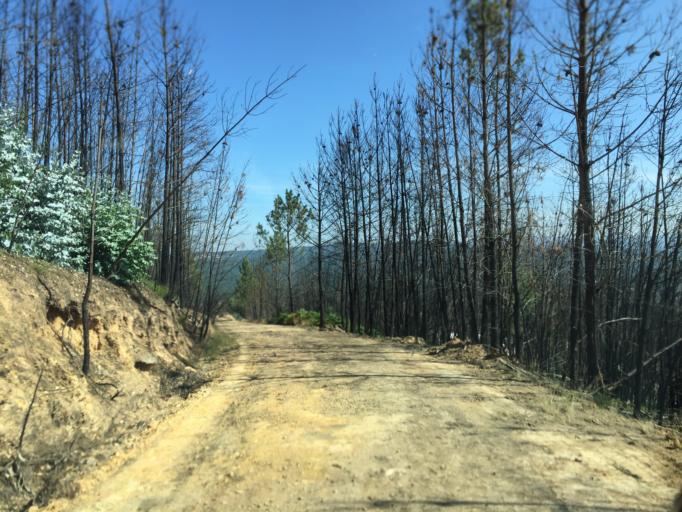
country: PT
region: Santarem
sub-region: Macao
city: Macao
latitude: 39.6579
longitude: -7.9848
